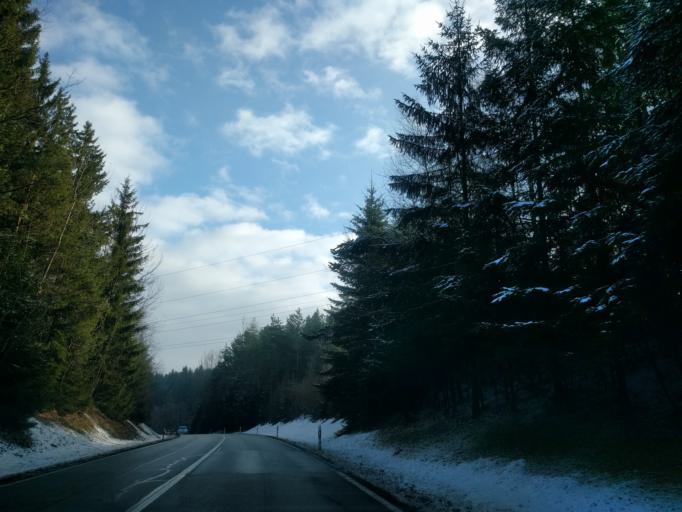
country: DE
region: Bavaria
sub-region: Lower Bavaria
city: Rinchnach
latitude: 48.9898
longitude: 13.1982
